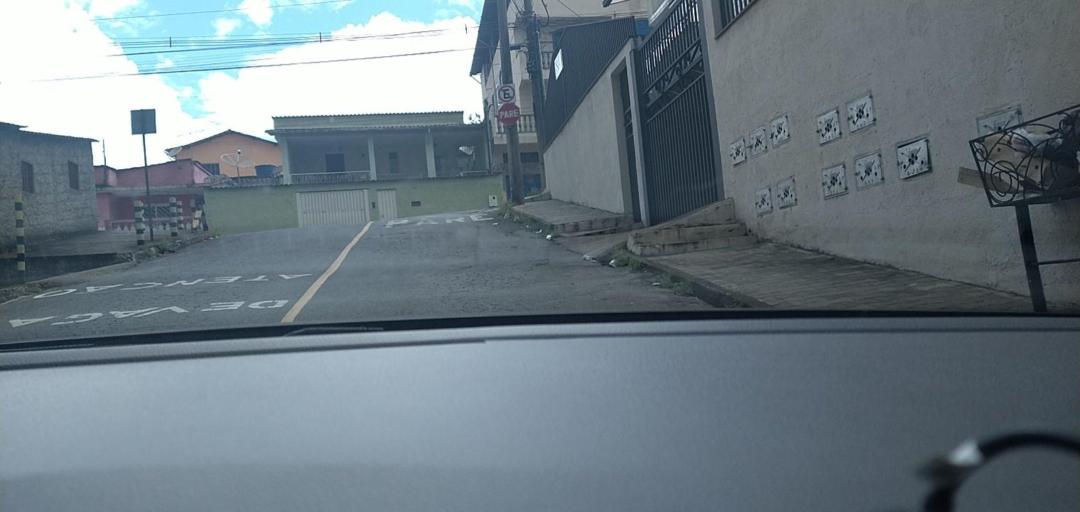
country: BR
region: Minas Gerais
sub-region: Joao Monlevade
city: Joao Monlevade
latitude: -19.8092
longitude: -43.1860
